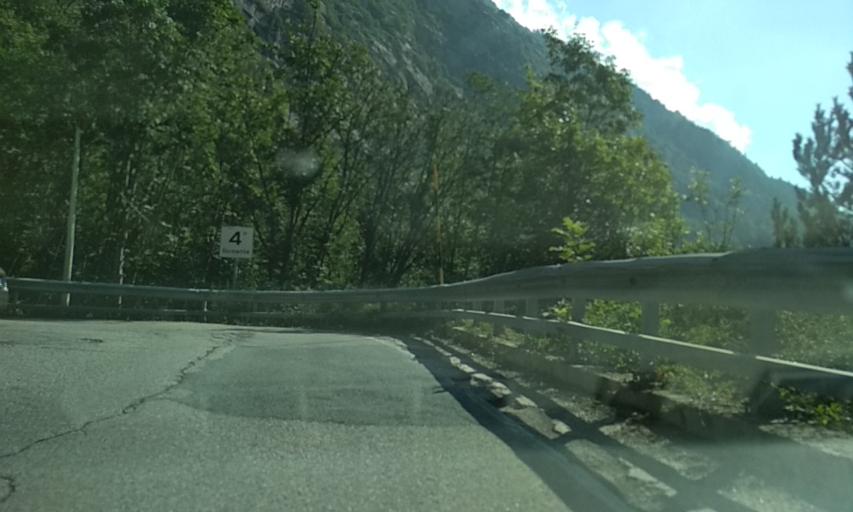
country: IT
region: Piedmont
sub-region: Provincia di Torino
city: Noasca
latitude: 45.4546
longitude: 7.3114
